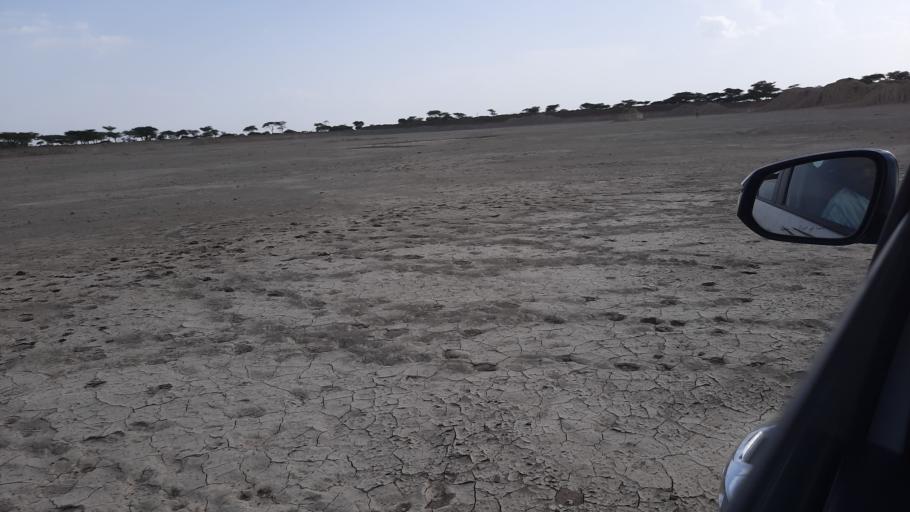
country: ET
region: Oromiya
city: Ziway
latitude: 7.6699
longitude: 38.6785
